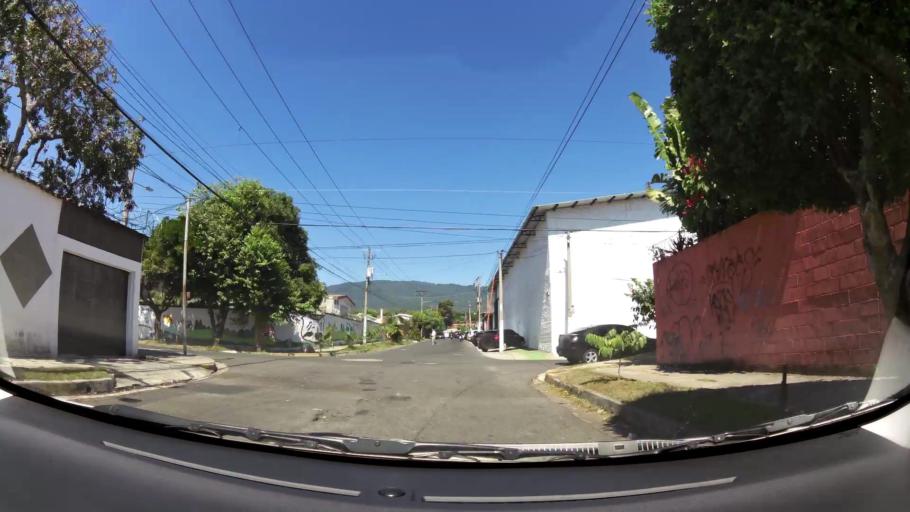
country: SV
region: La Libertad
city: Santa Tecla
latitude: 13.6706
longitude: -89.2814
